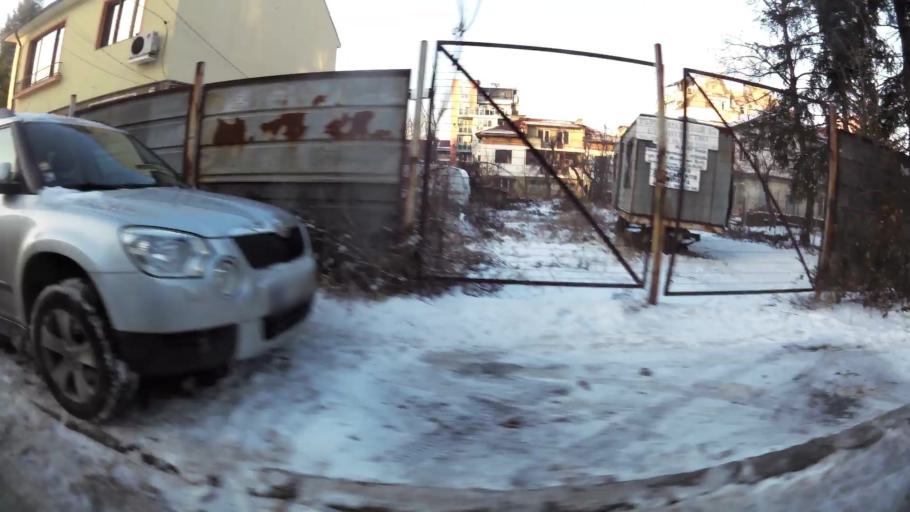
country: BG
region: Sofia-Capital
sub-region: Stolichna Obshtina
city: Sofia
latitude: 42.6943
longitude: 23.3617
